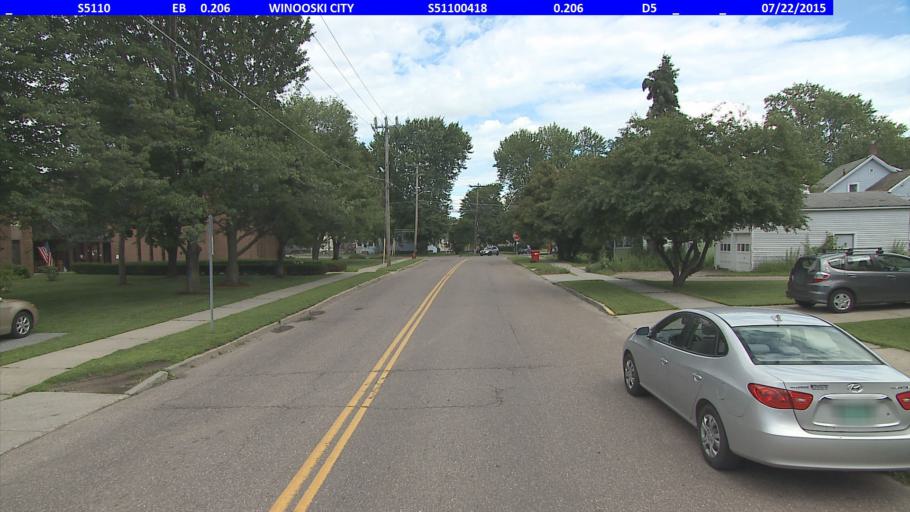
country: US
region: Vermont
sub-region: Chittenden County
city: Winooski
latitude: 44.4951
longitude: -73.1886
